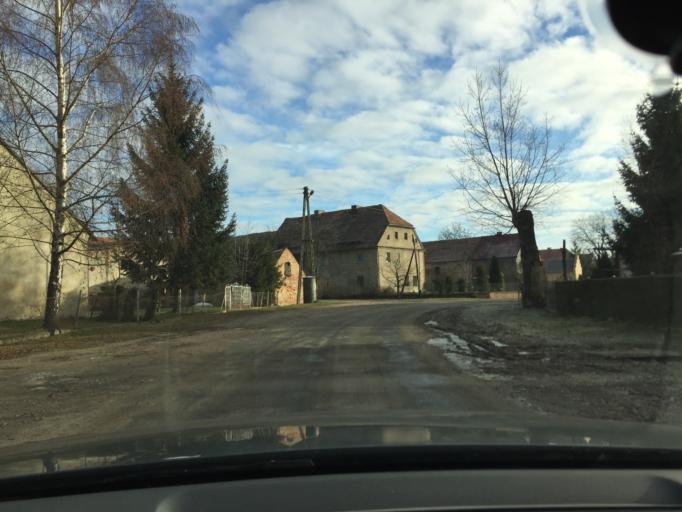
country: PL
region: Lower Silesian Voivodeship
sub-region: Powiat sredzki
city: Udanin
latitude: 51.0576
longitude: 16.4874
